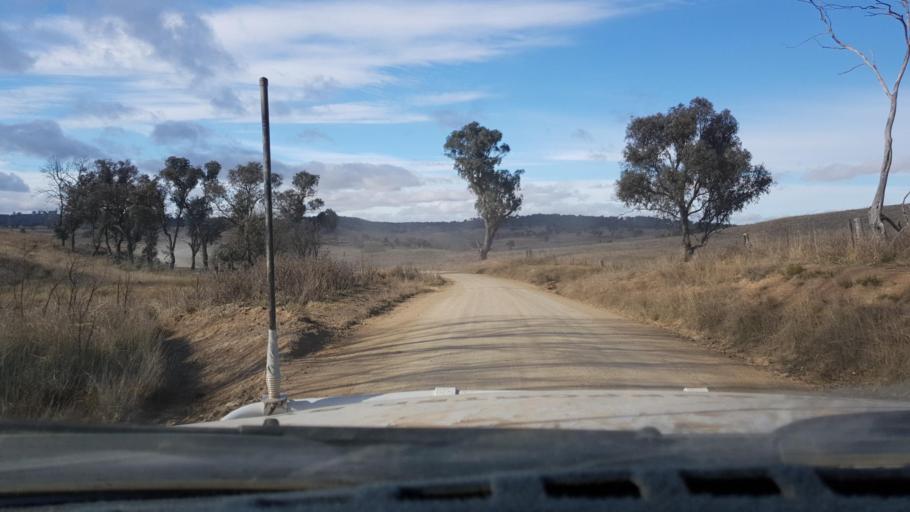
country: AU
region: New South Wales
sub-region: Armidale Dumaresq
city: Enmore
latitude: -30.7614
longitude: 151.6319
